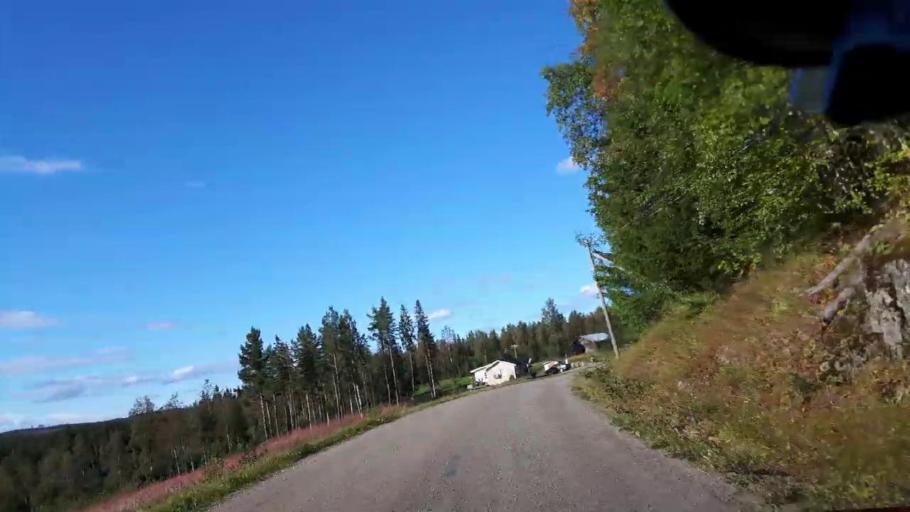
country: SE
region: Jaemtland
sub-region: Ragunda Kommun
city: Hammarstrand
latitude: 63.5002
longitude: 16.0346
